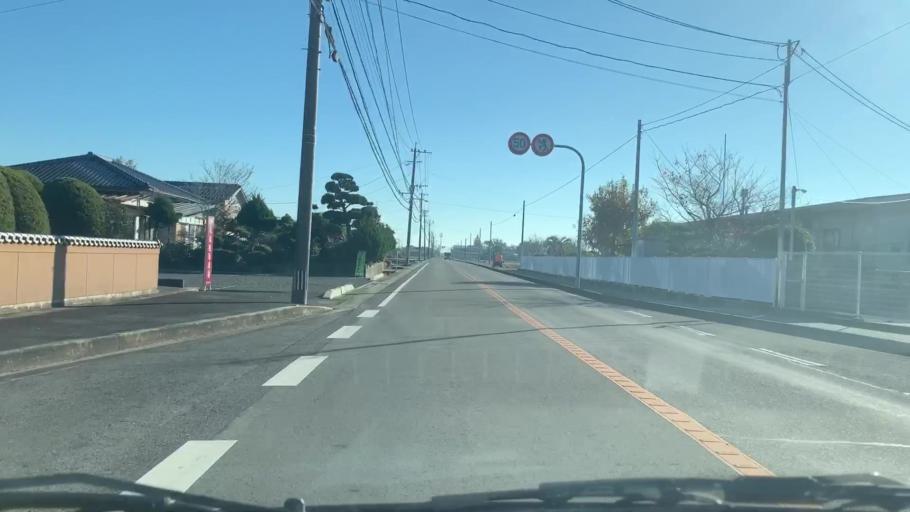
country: JP
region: Saga Prefecture
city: Kashima
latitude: 33.1840
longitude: 130.1661
